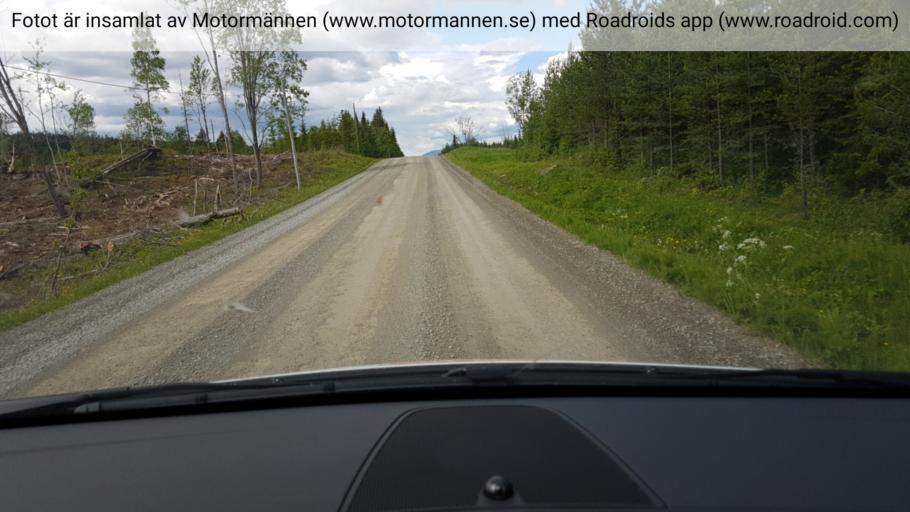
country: SE
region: Jaemtland
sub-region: Bergs Kommun
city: Hoverberg
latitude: 62.9875
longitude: 14.1825
